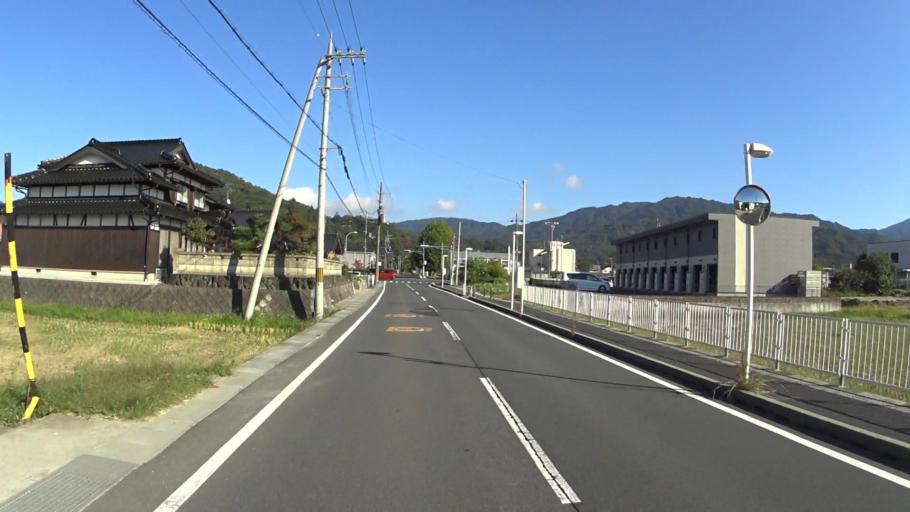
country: JP
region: Kyoto
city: Miyazu
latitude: 35.5320
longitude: 135.1206
